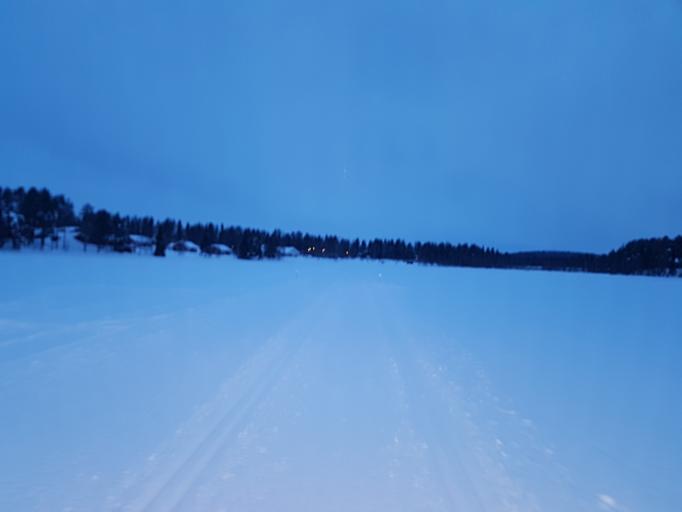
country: FI
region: Lapland
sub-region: Tunturi-Lappi
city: Kolari
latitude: 67.6094
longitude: 24.1430
